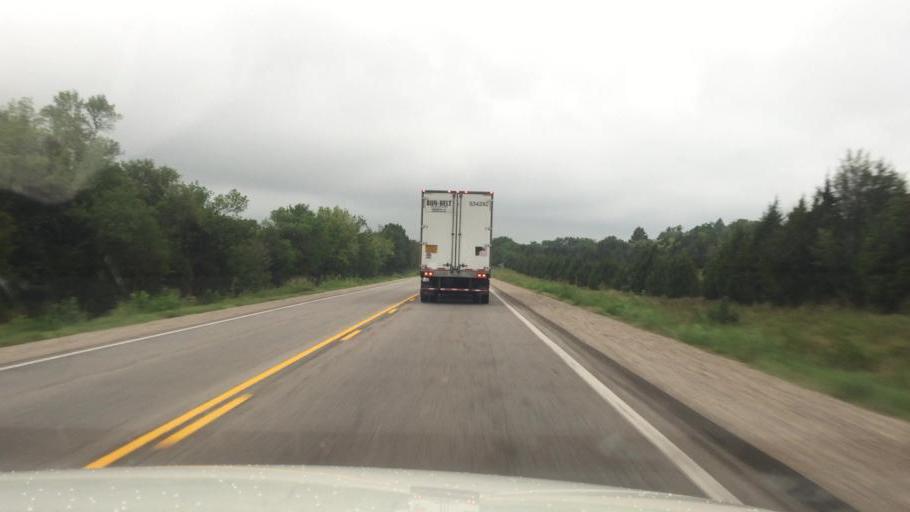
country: US
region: Kansas
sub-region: Montgomery County
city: Coffeyville
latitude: 37.1472
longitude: -95.5769
